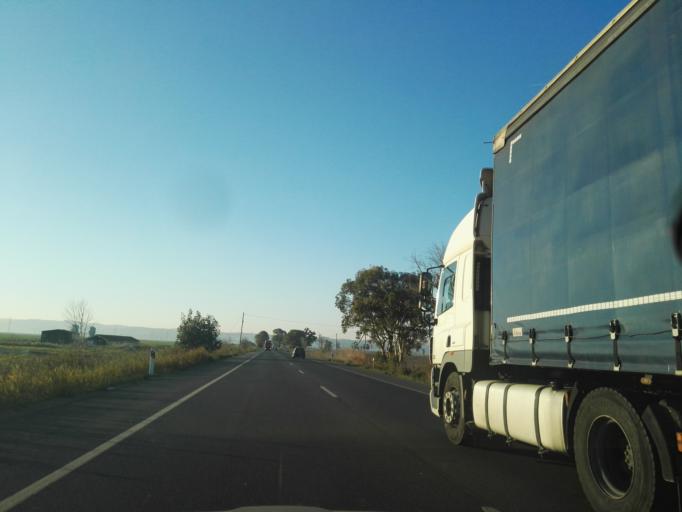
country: PT
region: Santarem
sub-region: Benavente
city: Samora Correia
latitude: 38.9280
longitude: -8.9018
